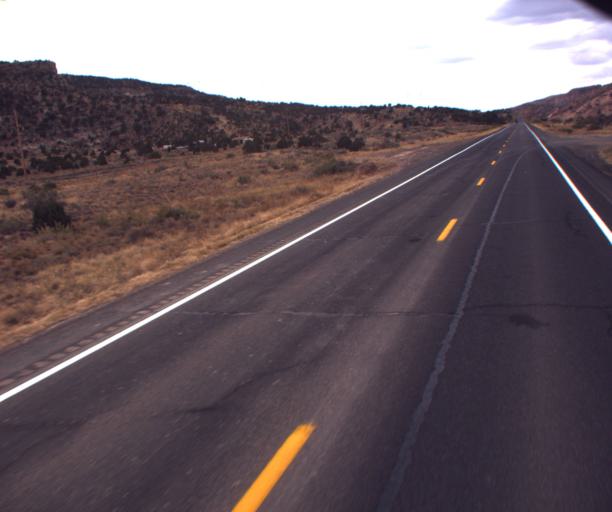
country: US
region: Arizona
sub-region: Navajo County
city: Kayenta
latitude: 36.6695
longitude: -110.4055
